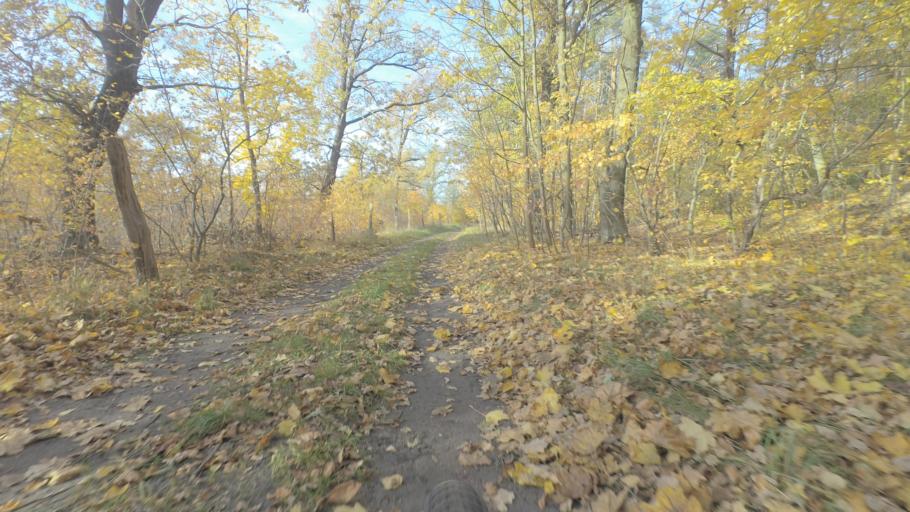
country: DE
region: Brandenburg
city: Trebbin
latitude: 52.2312
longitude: 13.2881
